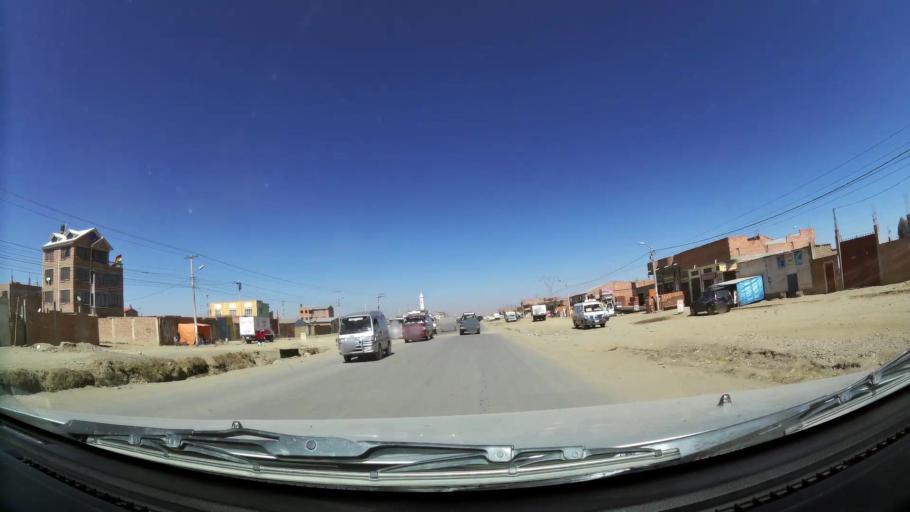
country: BO
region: La Paz
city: La Paz
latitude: -16.5756
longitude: -68.2286
